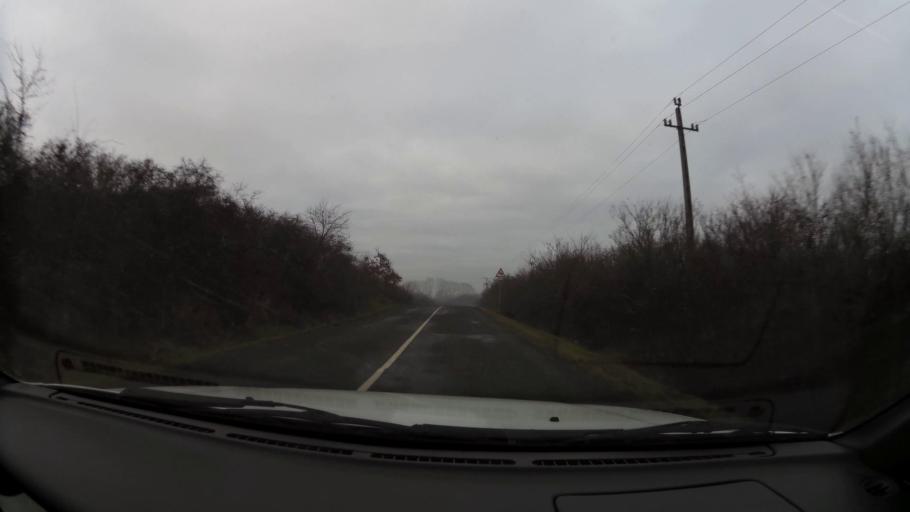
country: HU
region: Borsod-Abauj-Zemplen
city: Rudabanya
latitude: 48.3849
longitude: 20.6218
